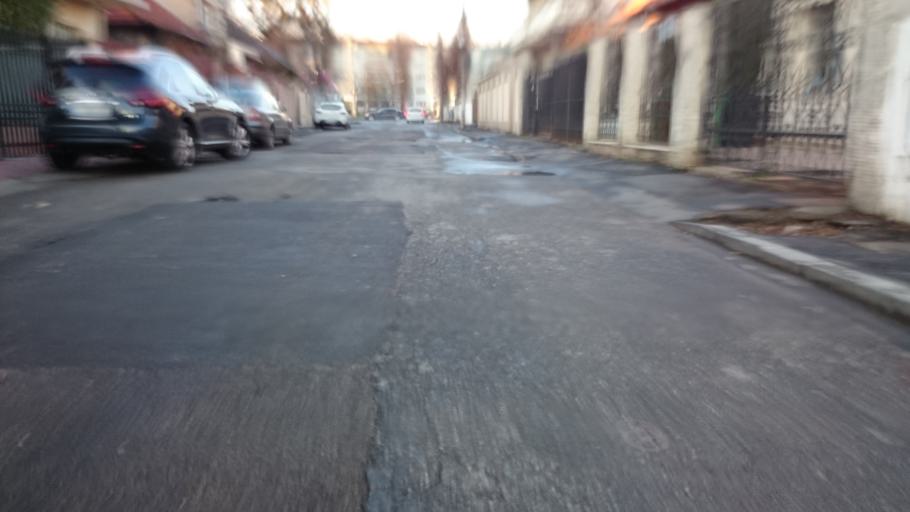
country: RO
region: Bucuresti
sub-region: Municipiul Bucuresti
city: Bucuresti
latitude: 44.4256
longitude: 26.0588
